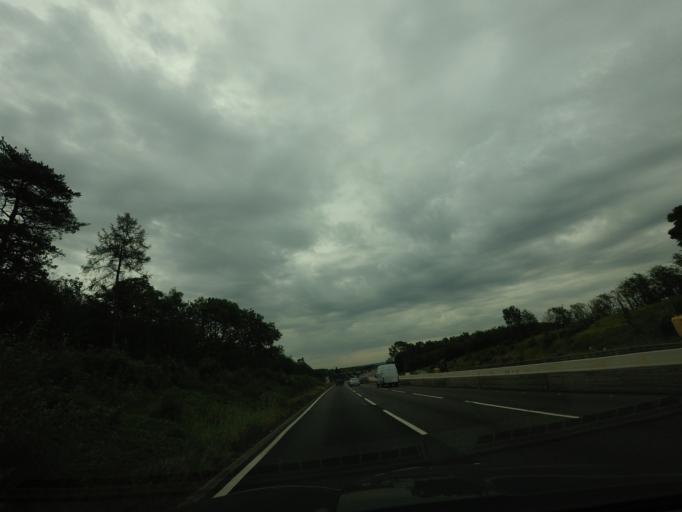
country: GB
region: England
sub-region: Milton Keynes
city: Gayhurst
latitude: 52.0975
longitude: -0.7628
